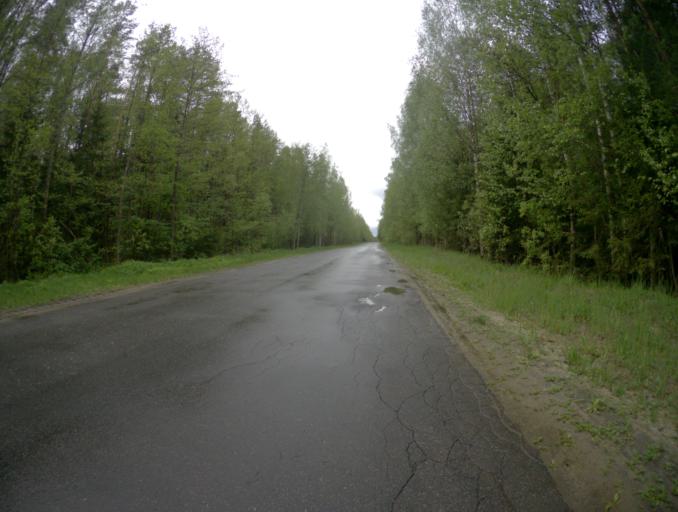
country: RU
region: Vladimir
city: Zolotkovo
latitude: 55.3459
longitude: 40.9785
